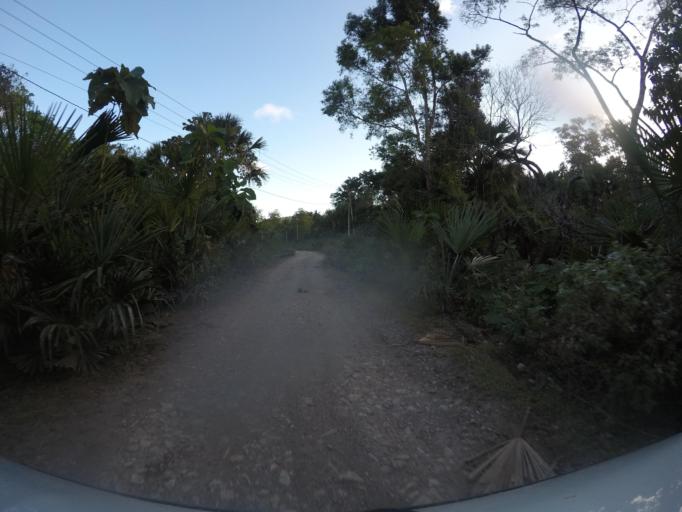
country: TL
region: Baucau
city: Venilale
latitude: -8.7243
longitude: 126.7089
